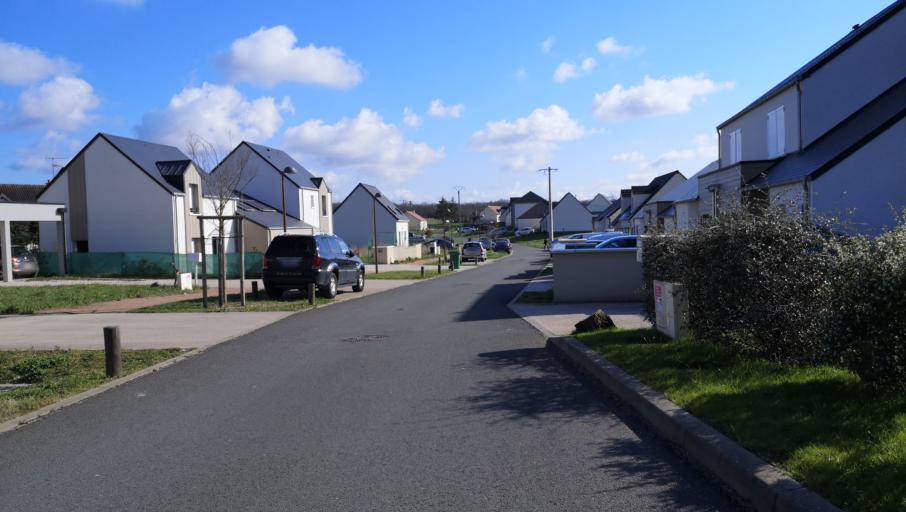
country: FR
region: Centre
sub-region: Departement du Loiret
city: Chanteau
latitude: 47.9637
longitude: 1.9714
